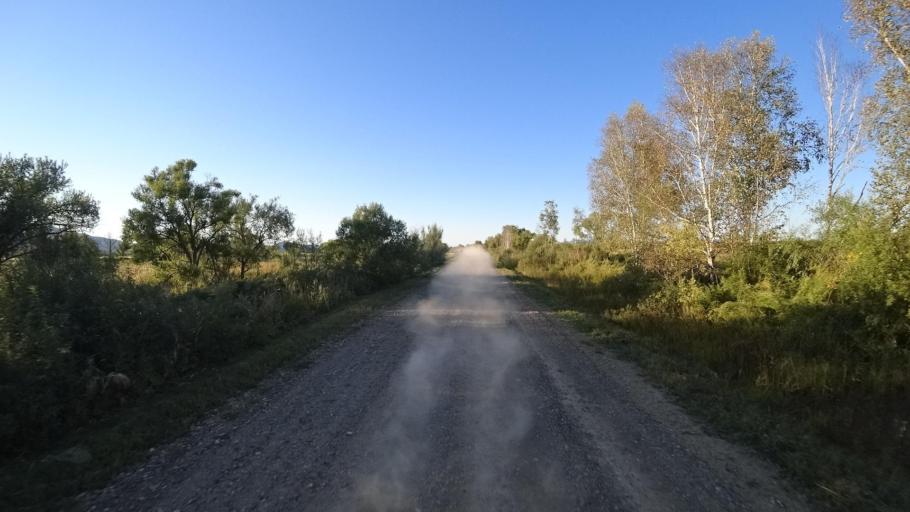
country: RU
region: Primorskiy
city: Kirovskiy
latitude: 44.7990
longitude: 133.6213
